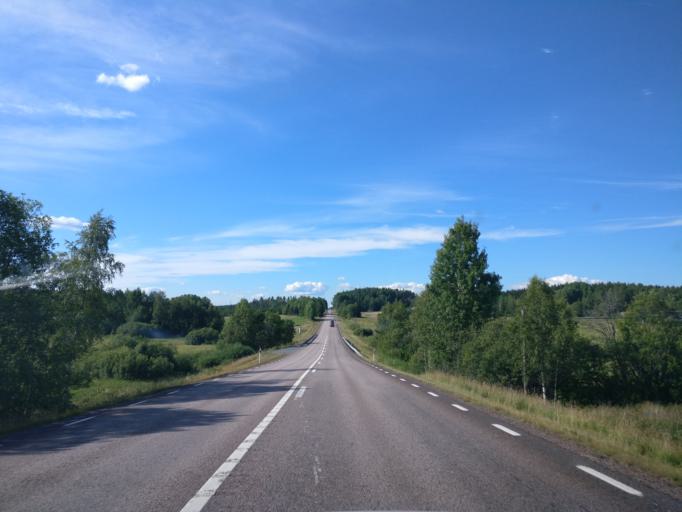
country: SE
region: Vaermland
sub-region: Karlstads Kommun
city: Edsvalla
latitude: 59.5770
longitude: 13.0191
